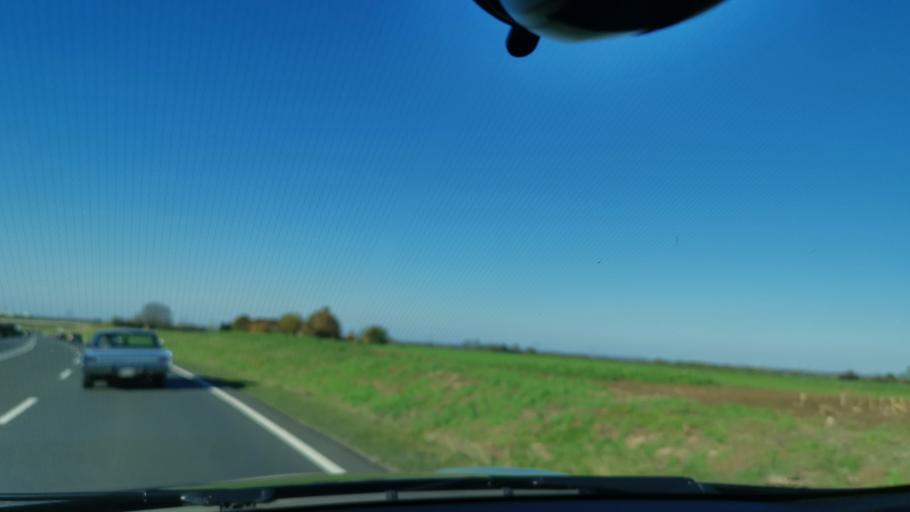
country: DE
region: North Rhine-Westphalia
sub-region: Regierungsbezirk Dusseldorf
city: Rommerskirchen
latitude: 51.0464
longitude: 6.6664
